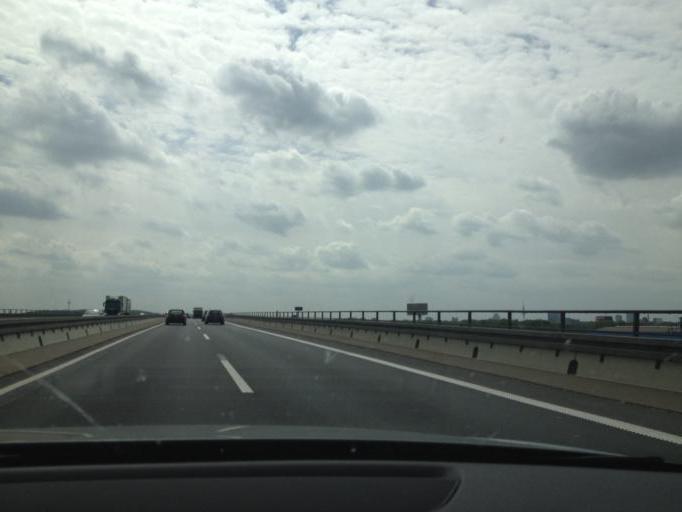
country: DE
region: North Rhine-Westphalia
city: Meiderich
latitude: 51.4580
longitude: 6.7745
